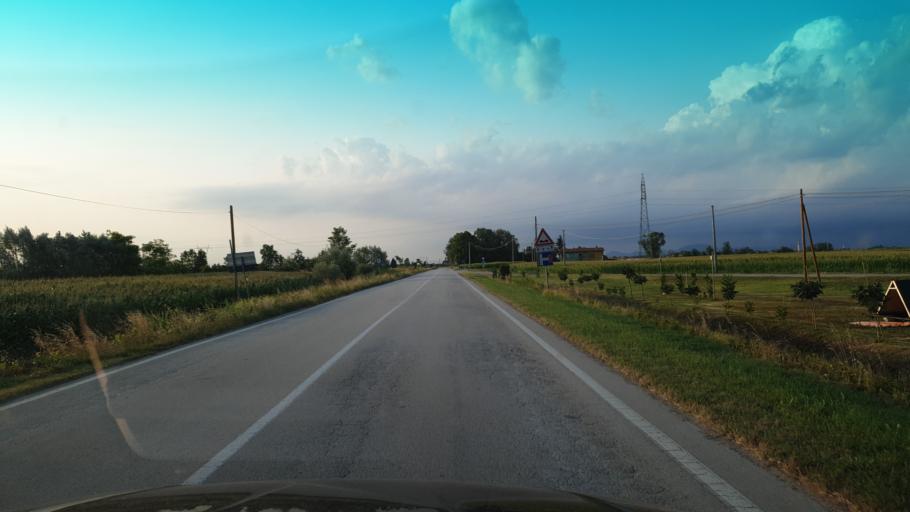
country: IT
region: Veneto
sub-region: Provincia di Rovigo
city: San Bellino
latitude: 45.0472
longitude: 11.5818
